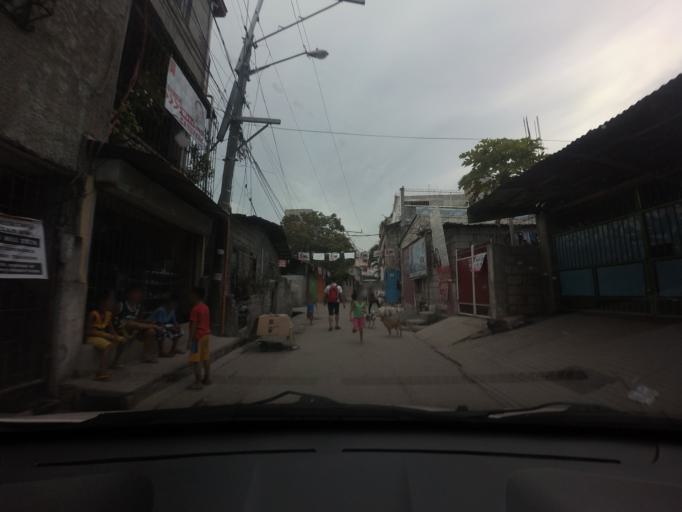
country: PH
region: Calabarzon
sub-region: Province of Rizal
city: Taguig
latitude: 14.5003
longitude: 121.0607
